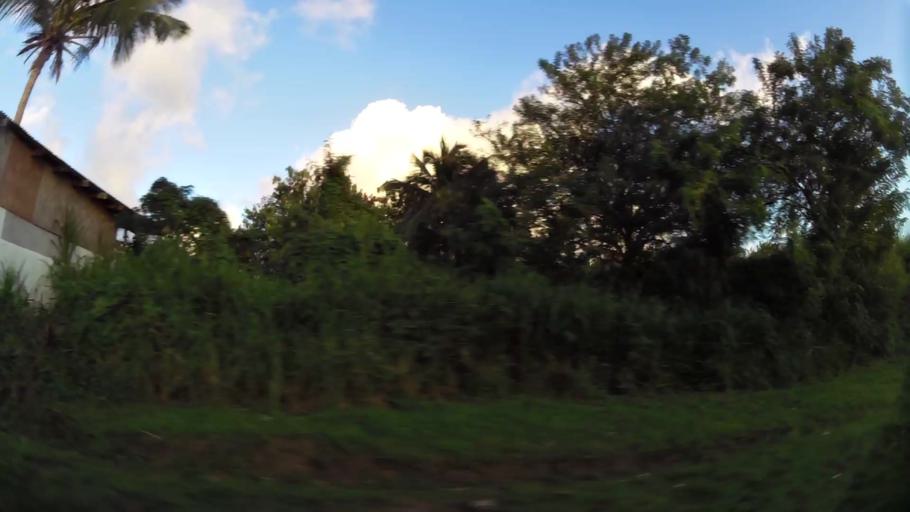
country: KN
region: Saint Anne Sandy Point
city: Sandy Point Town
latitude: 17.3837
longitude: -62.8532
